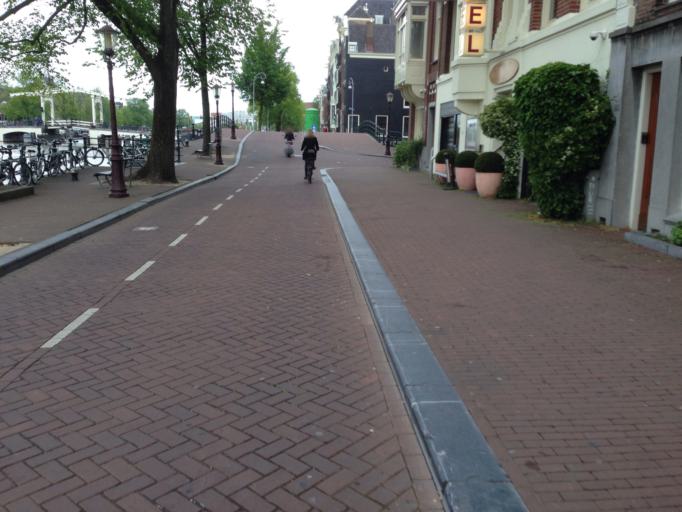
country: NL
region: North Holland
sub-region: Gemeente Amsterdam
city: Amsterdam
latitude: 52.3624
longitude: 4.9037
